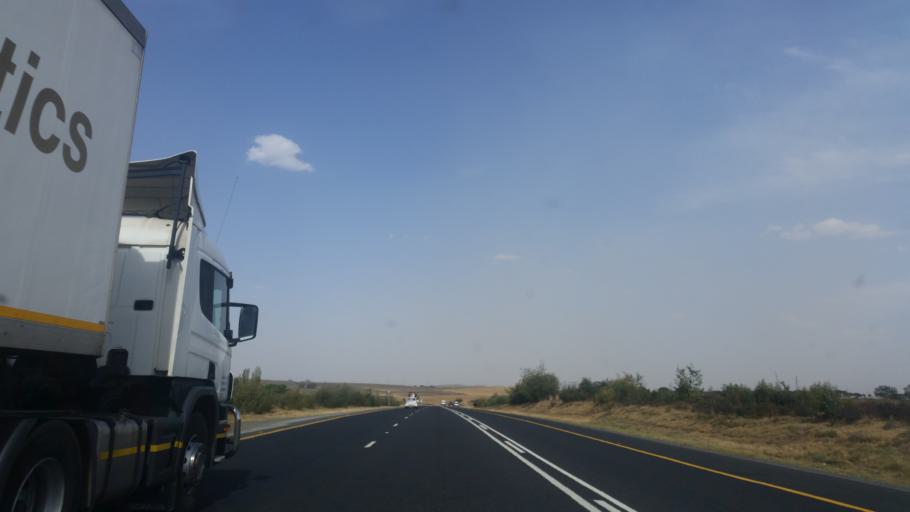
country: ZA
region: Orange Free State
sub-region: Thabo Mofutsanyana District Municipality
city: Bethlehem
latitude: -28.2978
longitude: 28.5406
